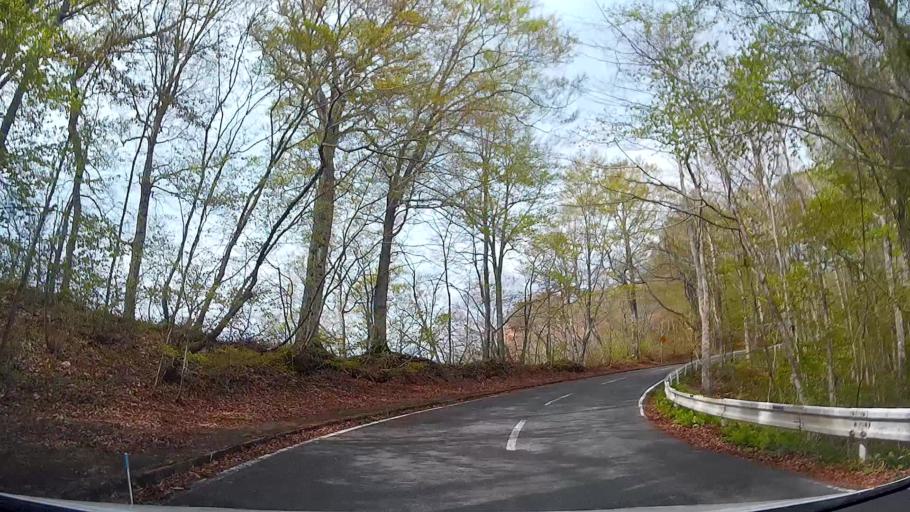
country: JP
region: Akita
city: Hanawa
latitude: 40.4381
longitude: 140.9166
